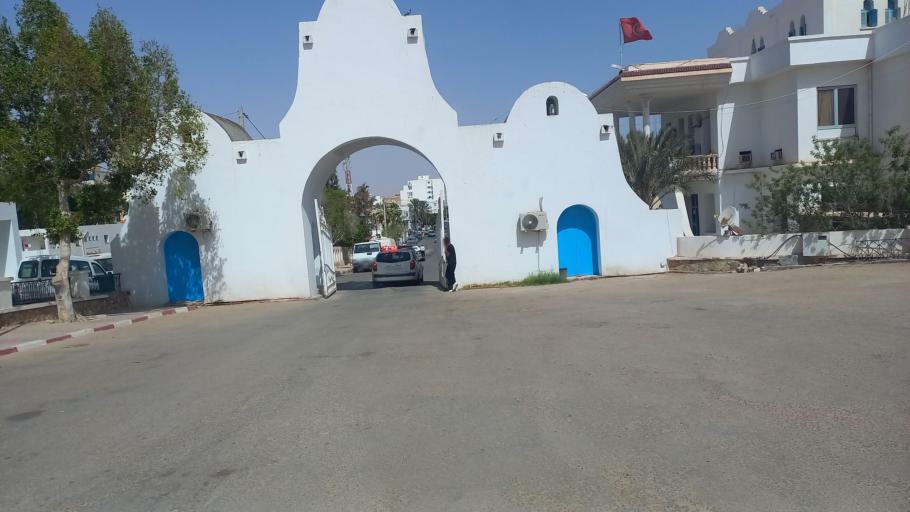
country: TN
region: Madanin
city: Medenine
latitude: 33.3420
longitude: 10.4924
